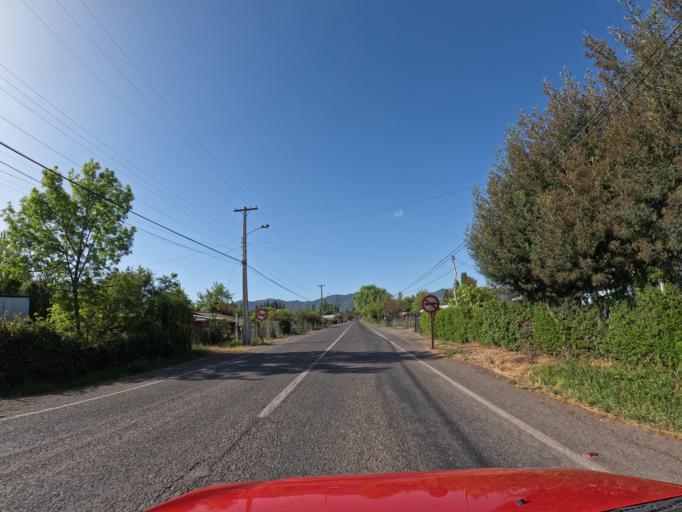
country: CL
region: Maule
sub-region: Provincia de Curico
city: Rauco
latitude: -34.8710
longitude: -71.2656
